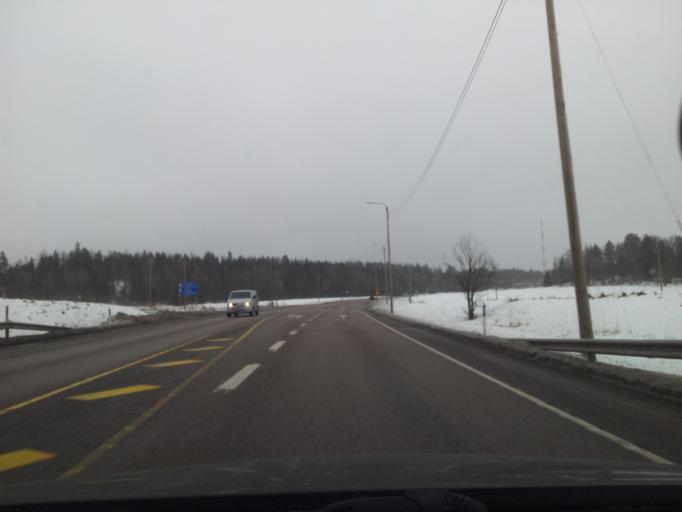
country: FI
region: Uusimaa
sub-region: Helsinki
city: Kirkkonummi
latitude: 60.1532
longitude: 24.5425
